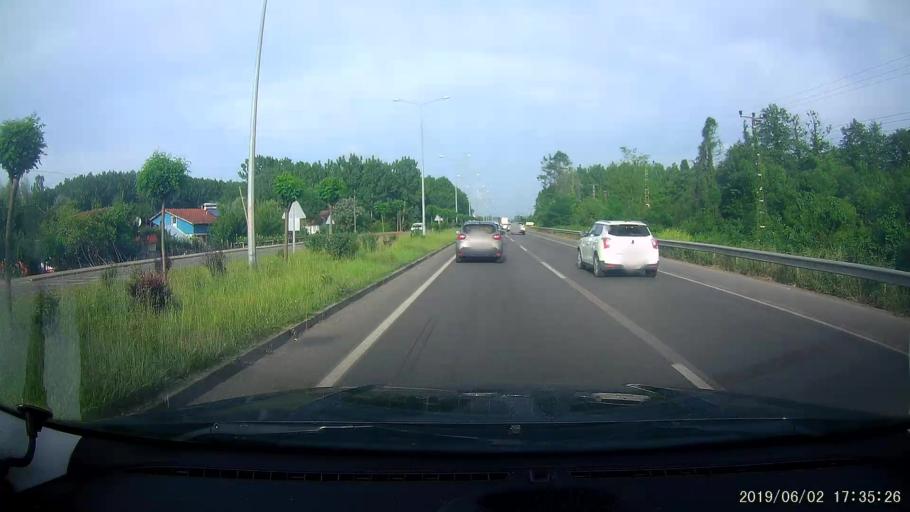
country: TR
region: Samsun
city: Terme
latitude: 41.2196
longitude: 36.8835
